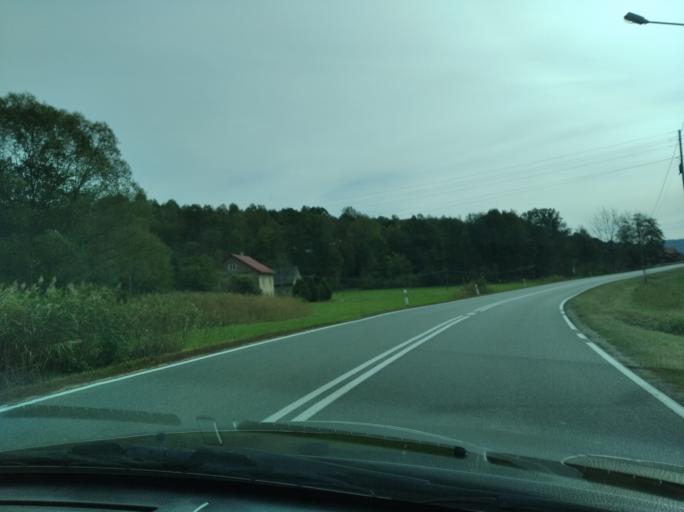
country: PL
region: Subcarpathian Voivodeship
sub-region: Powiat strzyzowski
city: Wisniowa
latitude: 49.8969
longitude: 21.6428
